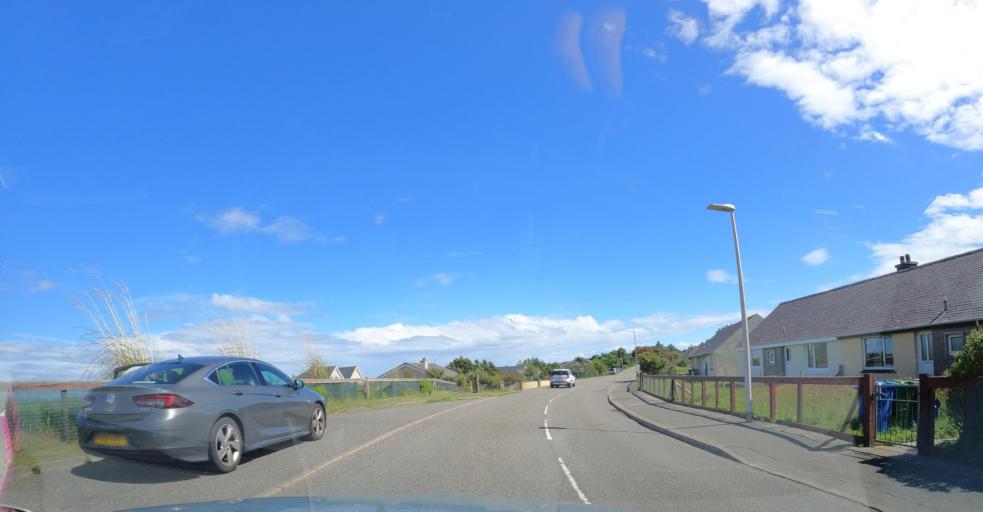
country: GB
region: Scotland
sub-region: Eilean Siar
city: Isle of Lewis
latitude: 58.2475
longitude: -6.3965
